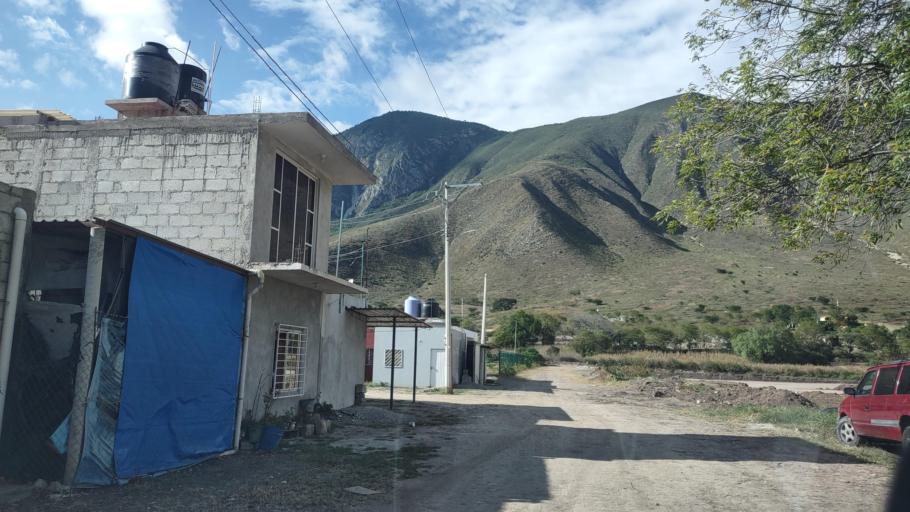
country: MX
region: Veracruz
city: Acultzingo
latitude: 18.7223
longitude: -97.3053
